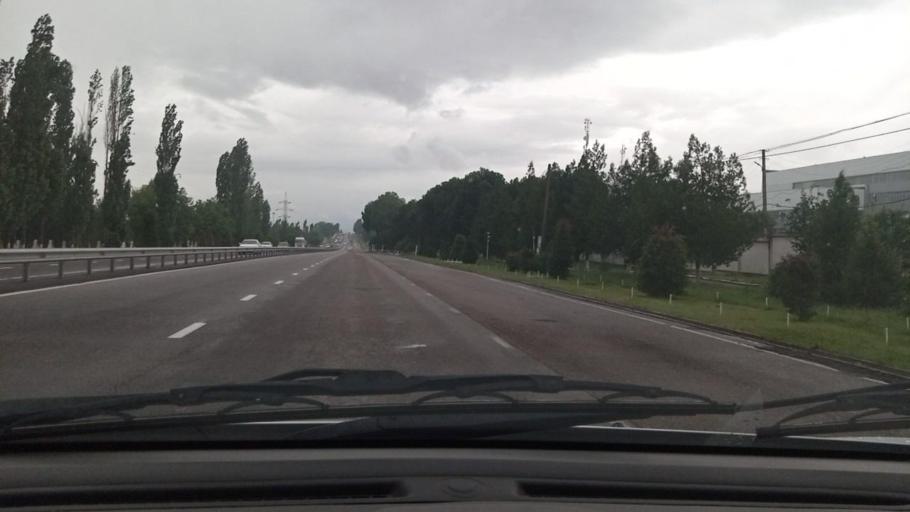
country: UZ
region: Toshkent
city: Angren
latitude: 40.9773
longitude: 70.0069
